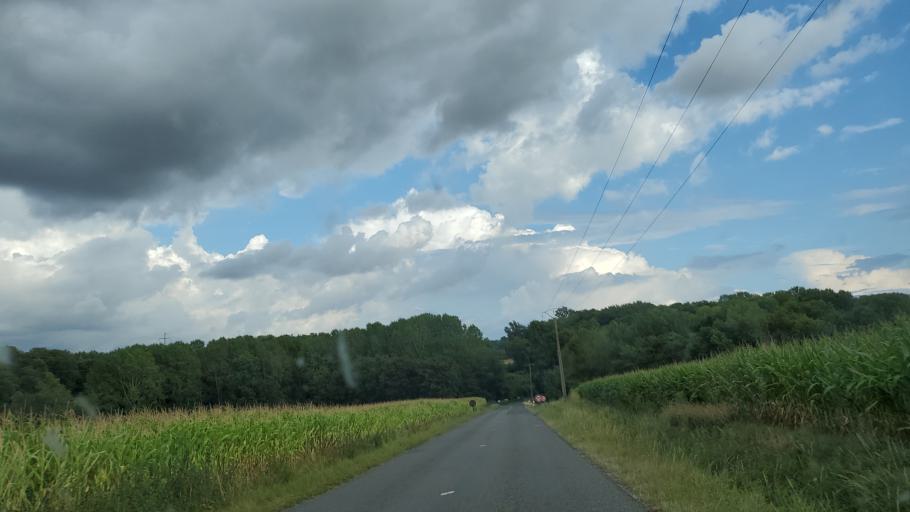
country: FR
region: Ile-de-France
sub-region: Departement de Seine-et-Marne
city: Chailly-en-Brie
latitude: 48.7800
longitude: 3.1679
